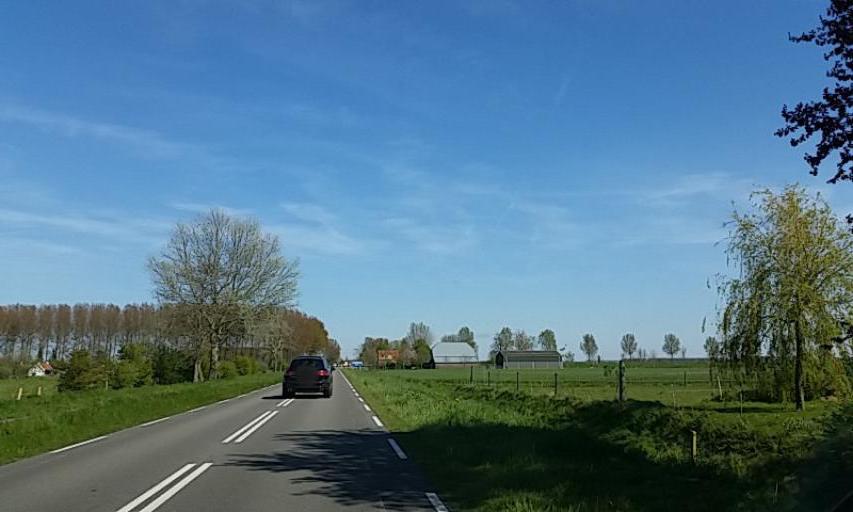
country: NL
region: Zeeland
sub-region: Gemeente Vlissingen
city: Vlissingen
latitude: 51.3748
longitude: 3.6351
